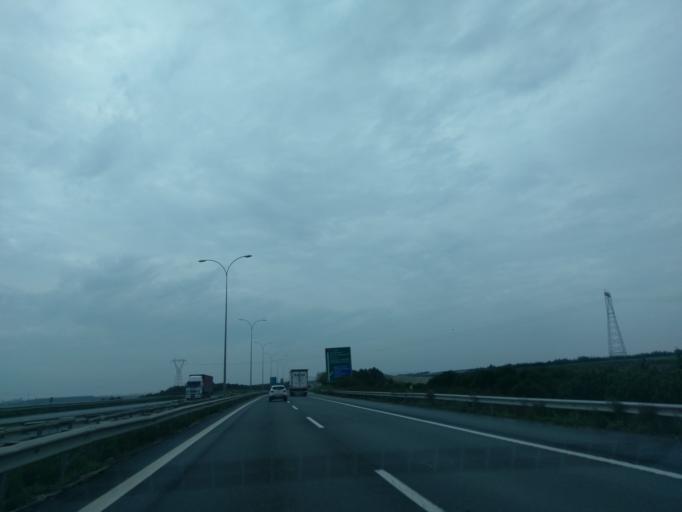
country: TR
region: Istanbul
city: Silivri
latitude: 41.1183
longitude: 28.2076
